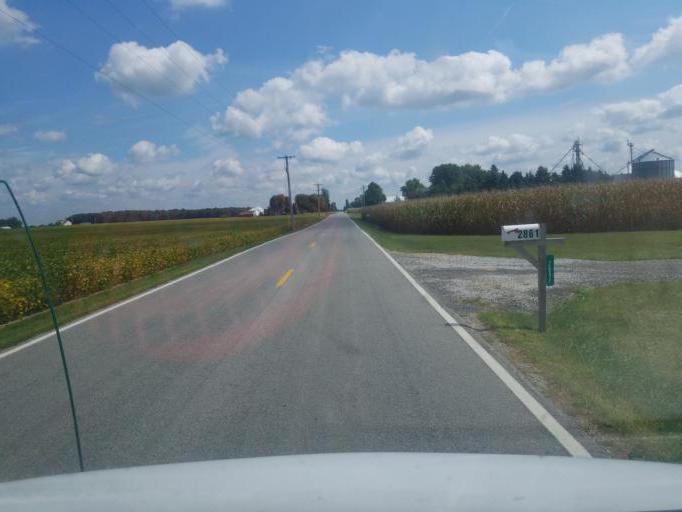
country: US
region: Ohio
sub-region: Marion County
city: Prospect
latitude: 40.3875
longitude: -83.1248
